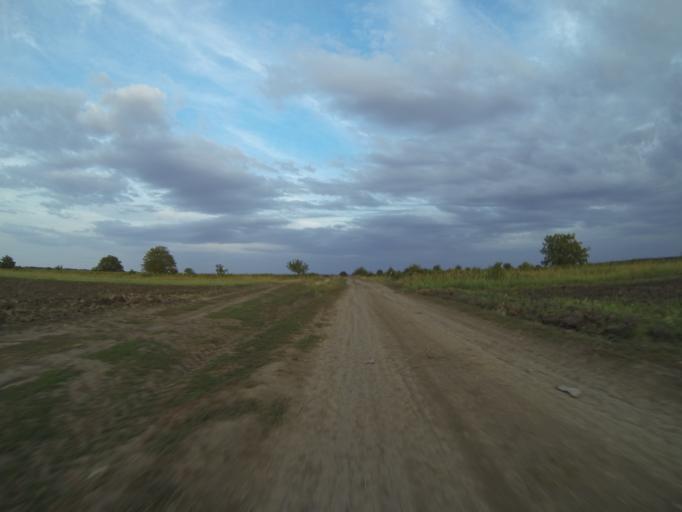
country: RO
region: Dolj
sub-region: Comuna Ceratu
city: Ceratu
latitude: 44.0997
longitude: 23.6804
